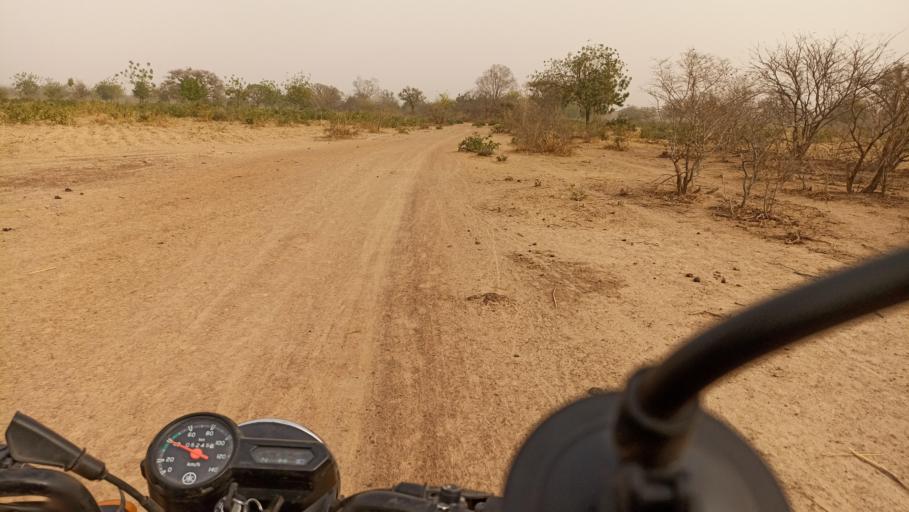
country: BF
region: Boucle du Mouhoun
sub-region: Province du Nayala
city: Toma
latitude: 12.8709
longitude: -2.7545
